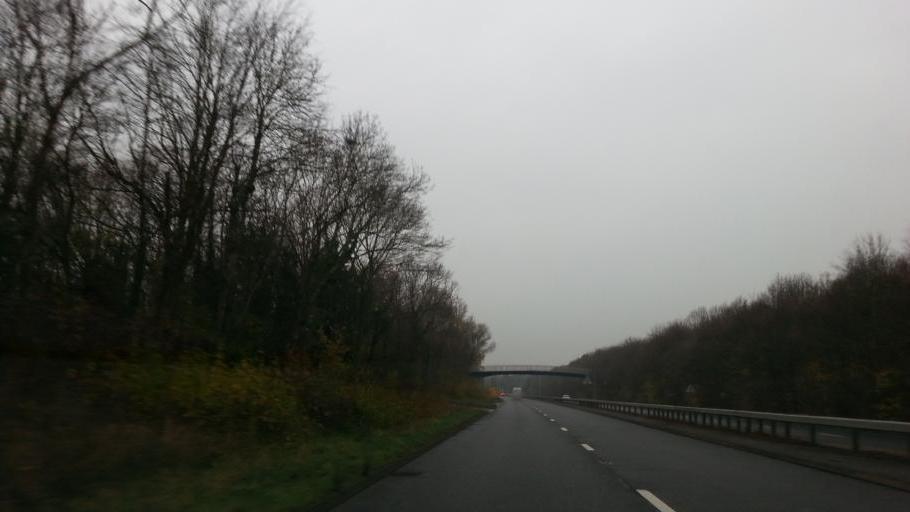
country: GB
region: England
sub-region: Peterborough
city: Castor
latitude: 52.5480
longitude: -0.3088
